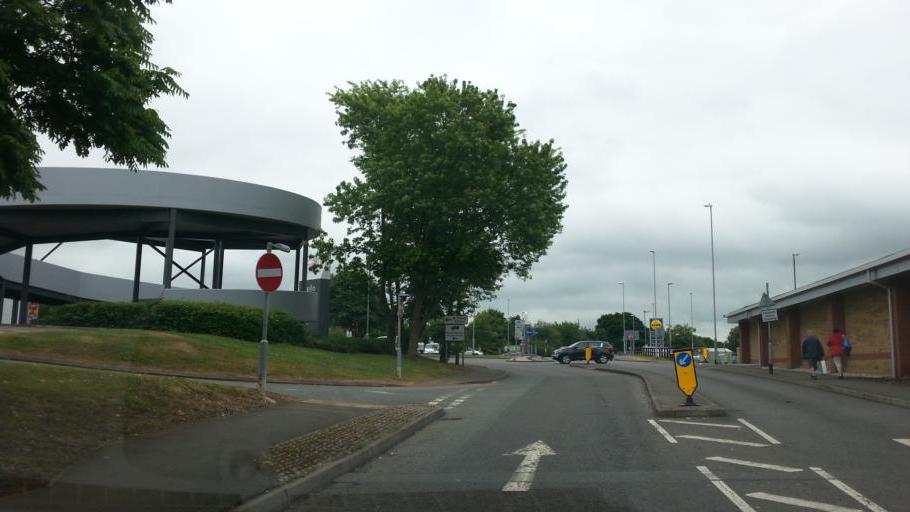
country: GB
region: England
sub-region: Northamptonshire
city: Northampton
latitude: 52.2558
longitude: -0.8358
